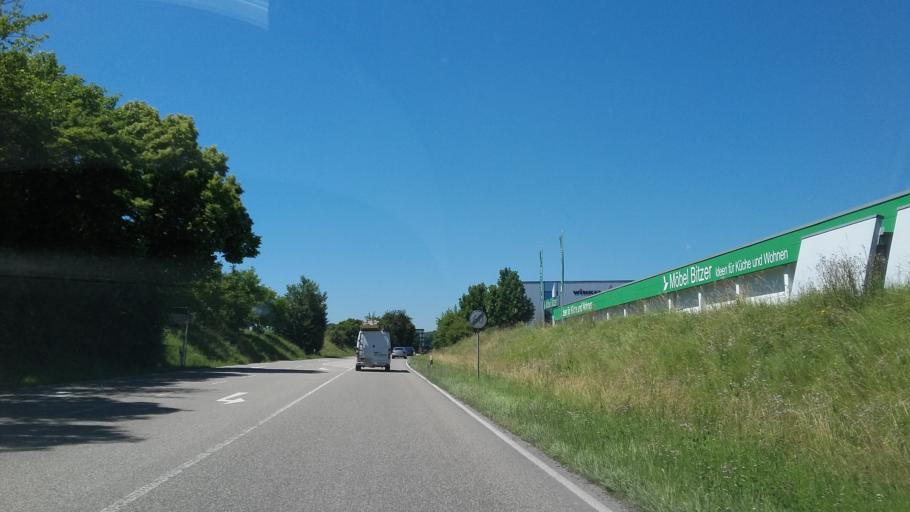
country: DE
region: Baden-Wuerttemberg
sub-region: Karlsruhe Region
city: Illingen
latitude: 48.9540
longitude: 8.9096
